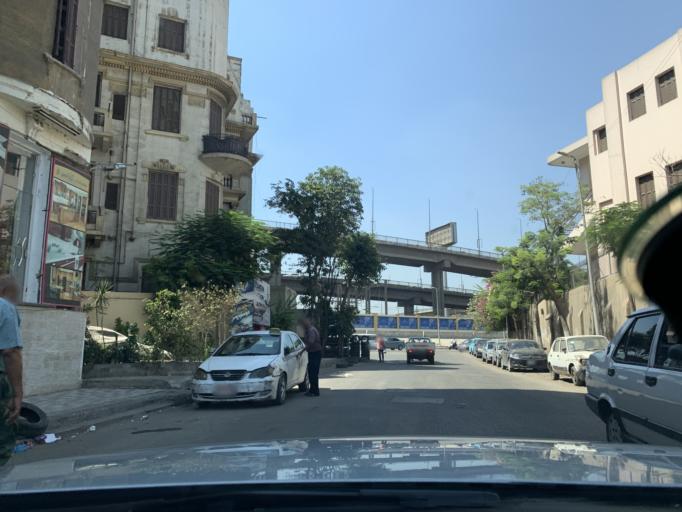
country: EG
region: Muhafazat al Qahirah
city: Cairo
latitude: 30.0691
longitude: 31.2665
